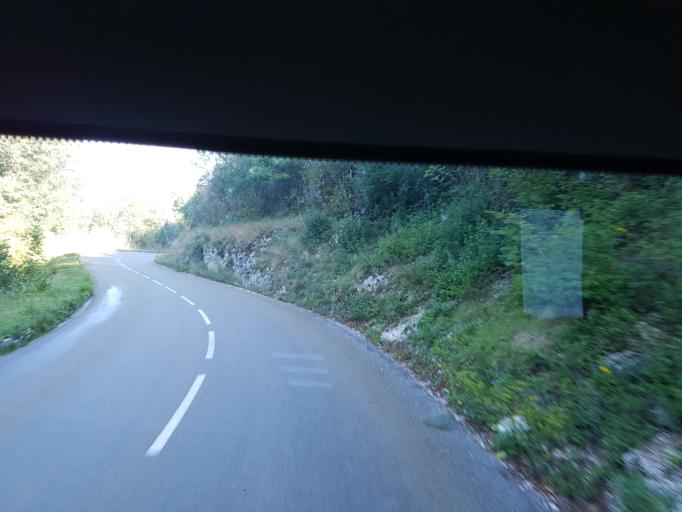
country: FR
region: Franche-Comte
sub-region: Departement du Jura
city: Orgelet
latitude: 46.4974
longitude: 5.6551
